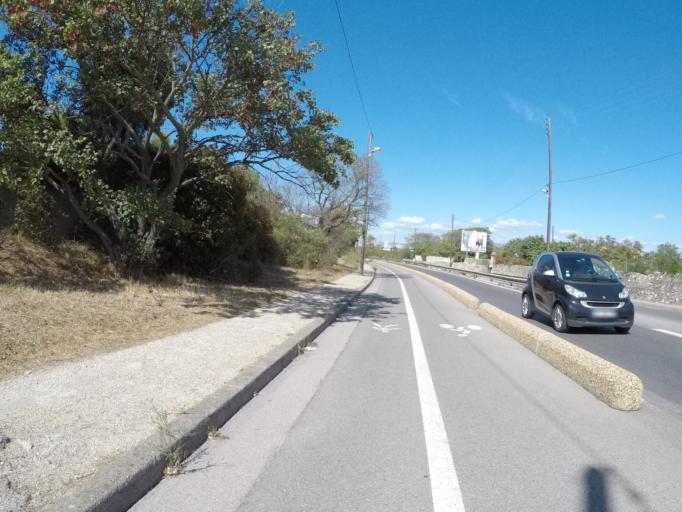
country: FR
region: Provence-Alpes-Cote d'Azur
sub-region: Departement des Bouches-du-Rhone
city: Marseille 09
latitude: 43.2368
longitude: 5.3988
